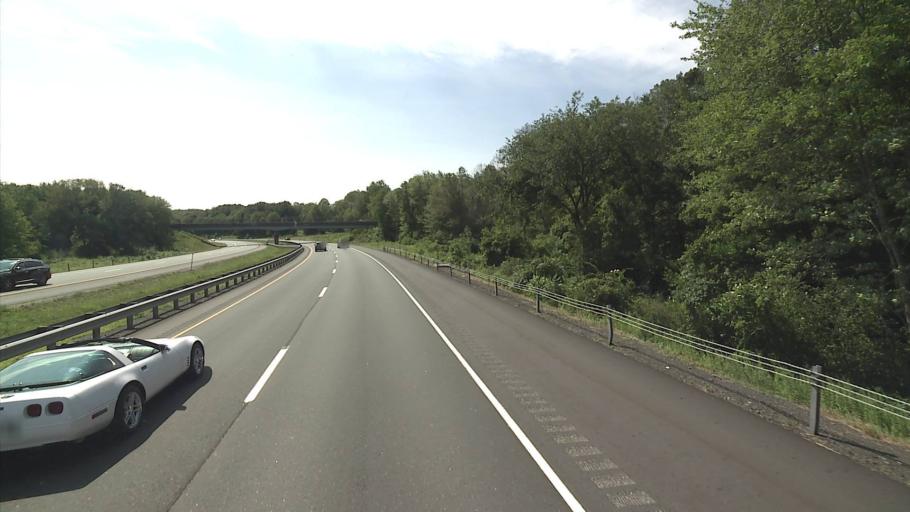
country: US
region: Connecticut
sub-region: Hartford County
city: Terramuggus
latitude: 41.6114
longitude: -72.4339
